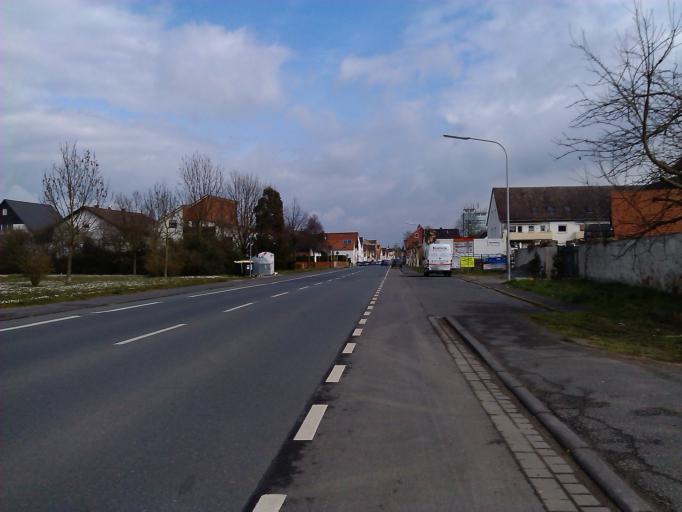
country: DE
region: Hesse
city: Pfungstadt
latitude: 49.7997
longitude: 8.5905
